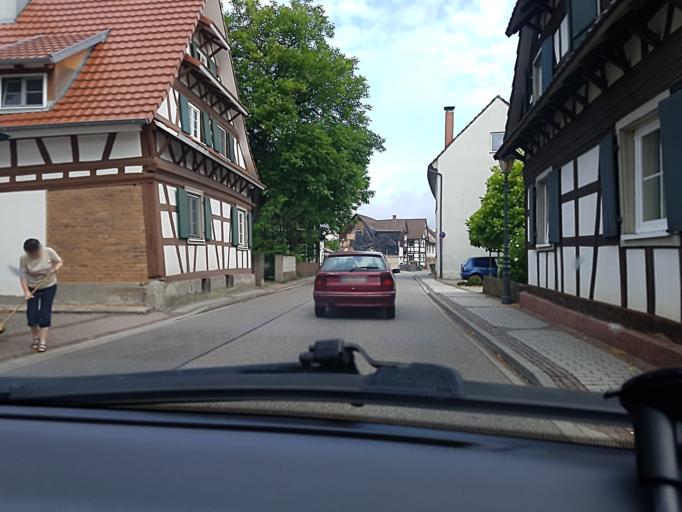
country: DE
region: Baden-Wuerttemberg
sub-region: Freiburg Region
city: Willstatt
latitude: 48.5422
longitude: 7.8918
